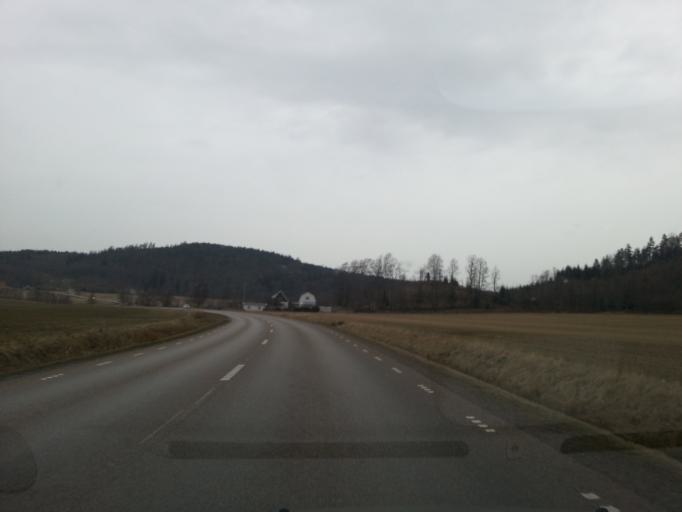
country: SE
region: Vaestra Goetaland
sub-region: Lilla Edets Kommun
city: Lilla Edet
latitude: 58.1392
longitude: 12.0990
